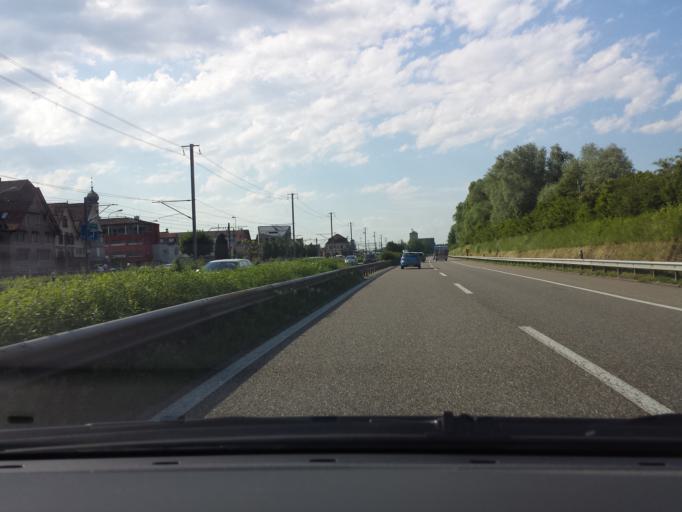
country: CH
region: Saint Gallen
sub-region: Wahlkreis Rheintal
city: Rheineck
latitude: 47.4645
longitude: 9.5945
